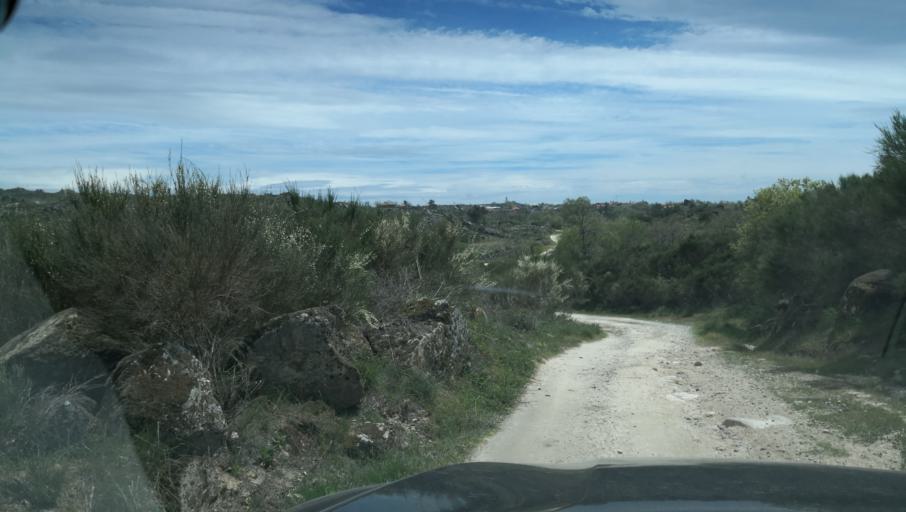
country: PT
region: Vila Real
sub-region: Vila Real
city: Vila Real
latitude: 41.3797
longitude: -7.6612
